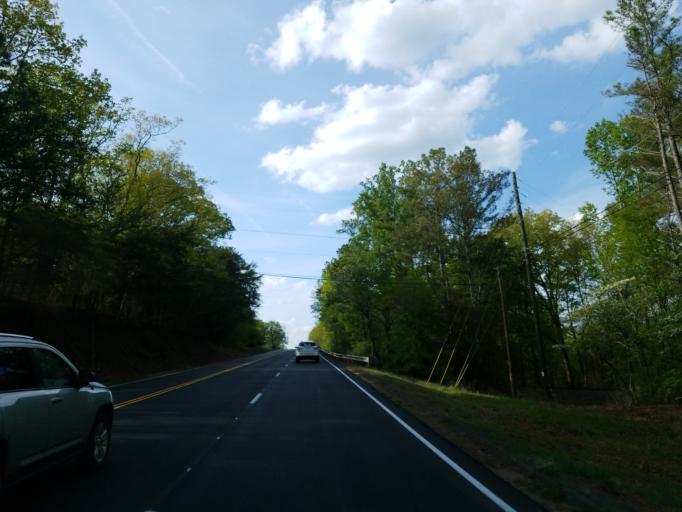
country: US
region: Georgia
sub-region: Pickens County
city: Jasper
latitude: 34.4462
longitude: -84.4019
